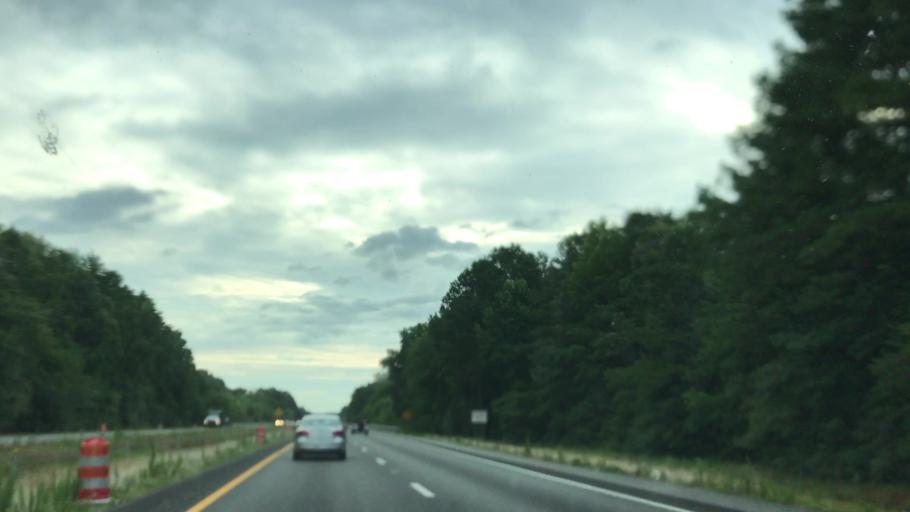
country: US
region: North Carolina
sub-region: Johnston County
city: Smithfield
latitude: 35.4748
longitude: -78.3717
